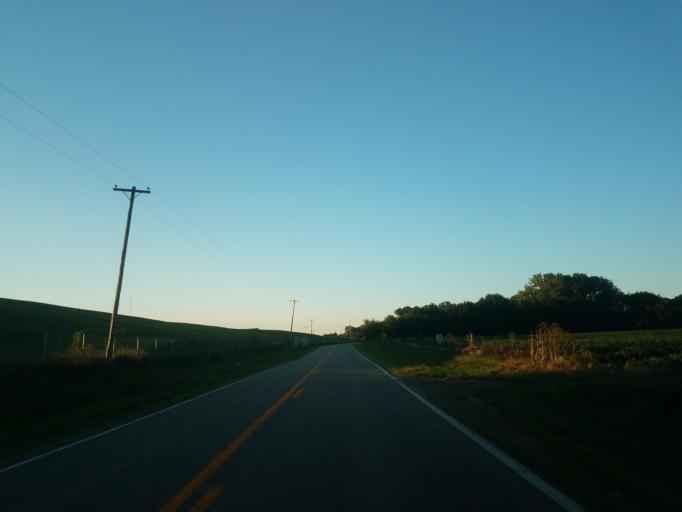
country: US
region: Illinois
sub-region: McLean County
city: Bloomington
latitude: 40.4624
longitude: -89.0348
